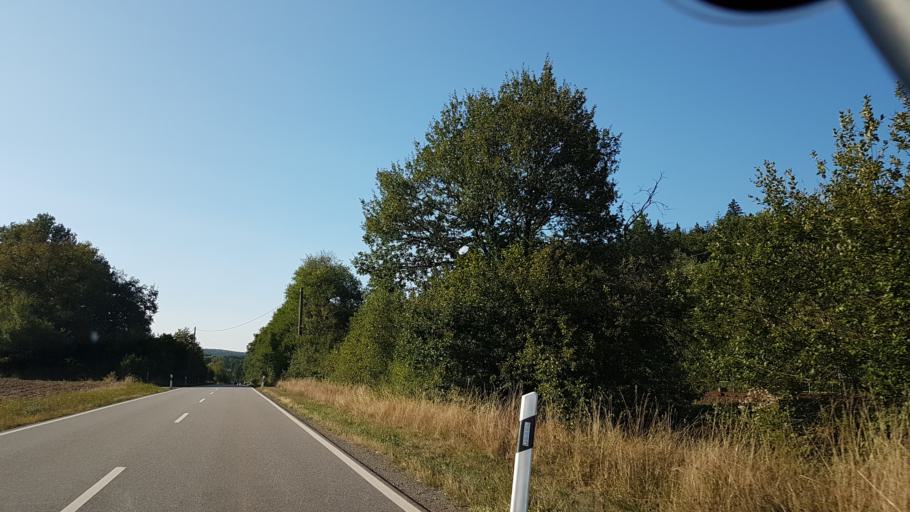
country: DE
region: Saarland
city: Nohfelden
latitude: 49.5702
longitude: 7.1179
